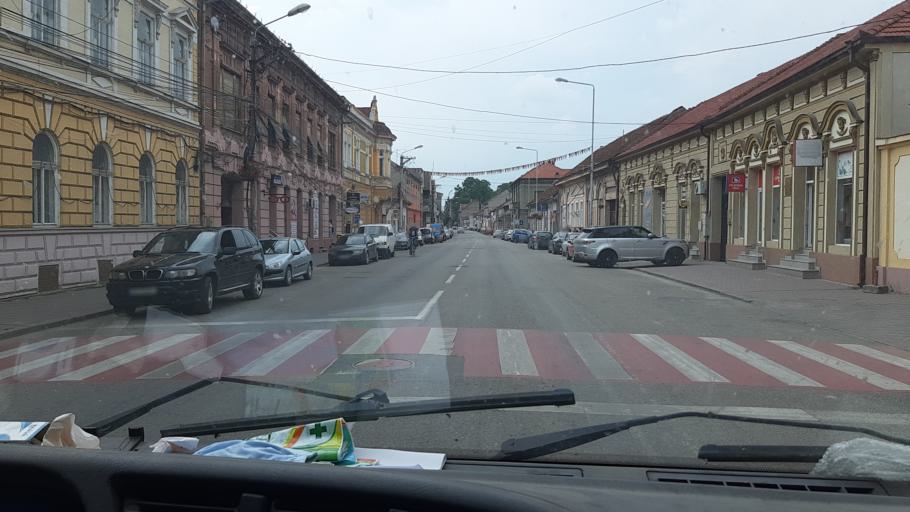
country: RO
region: Timis
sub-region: Municipiul Lugoj
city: Lugoj
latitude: 45.6836
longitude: 21.9014
